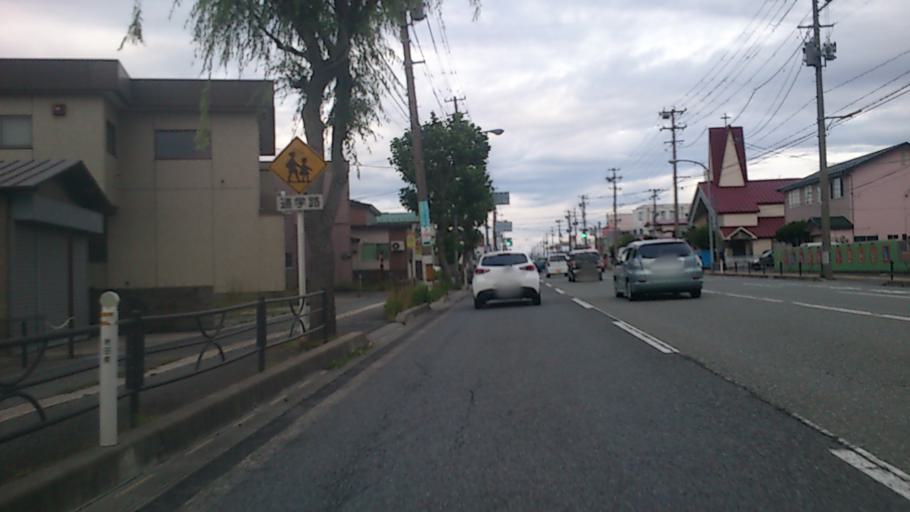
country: JP
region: Akita
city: Akita Shi
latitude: 39.7480
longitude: 140.0781
